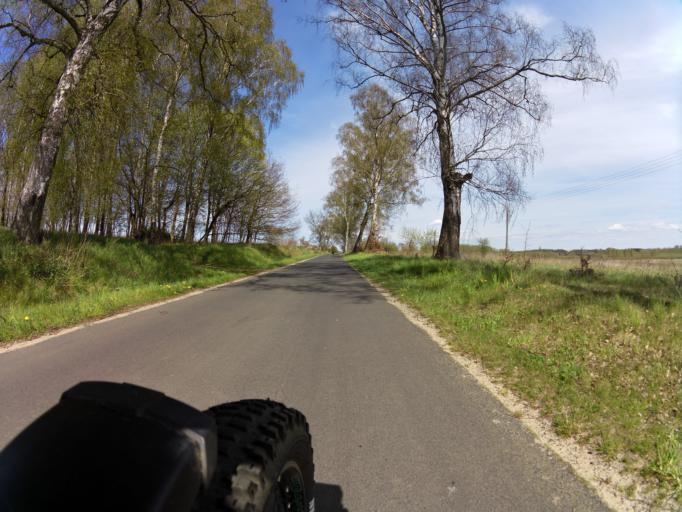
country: PL
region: West Pomeranian Voivodeship
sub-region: Powiat lobeski
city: Resko
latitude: 53.7880
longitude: 15.4261
